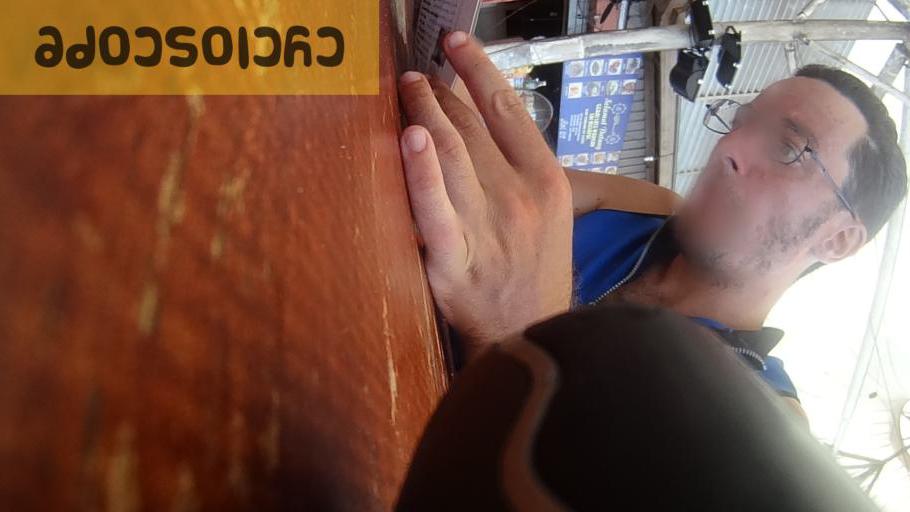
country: MY
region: Sabah
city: Beaufort
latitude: 5.0786
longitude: 115.5493
